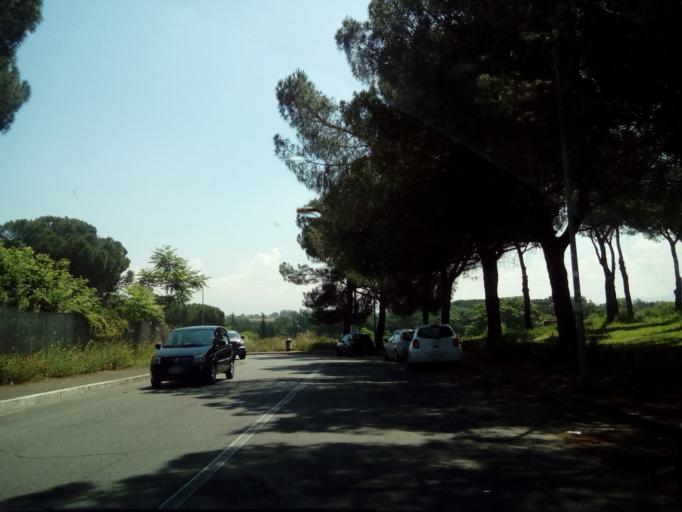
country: IT
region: Latium
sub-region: Citta metropolitana di Roma Capitale
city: Rome
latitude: 41.8809
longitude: 12.5897
